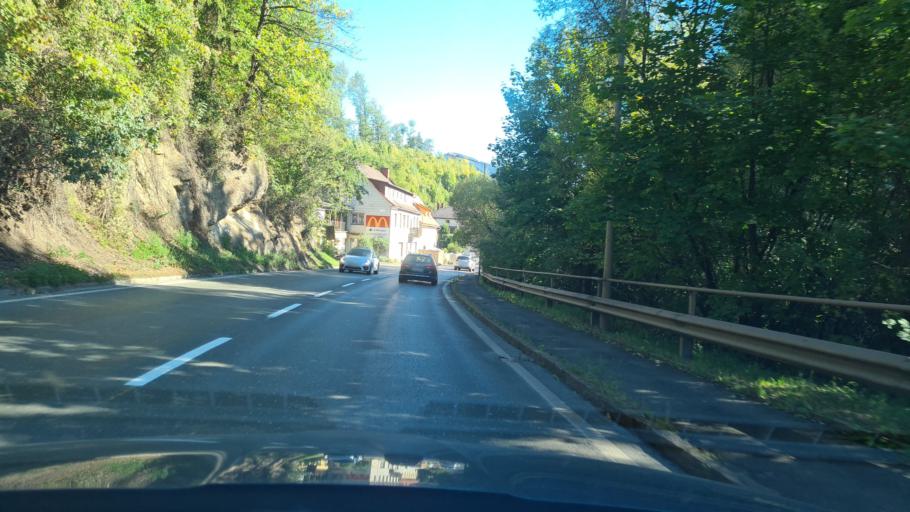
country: AT
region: Styria
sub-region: Politischer Bezirk Leoben
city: Leoben
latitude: 47.3788
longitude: 15.0787
